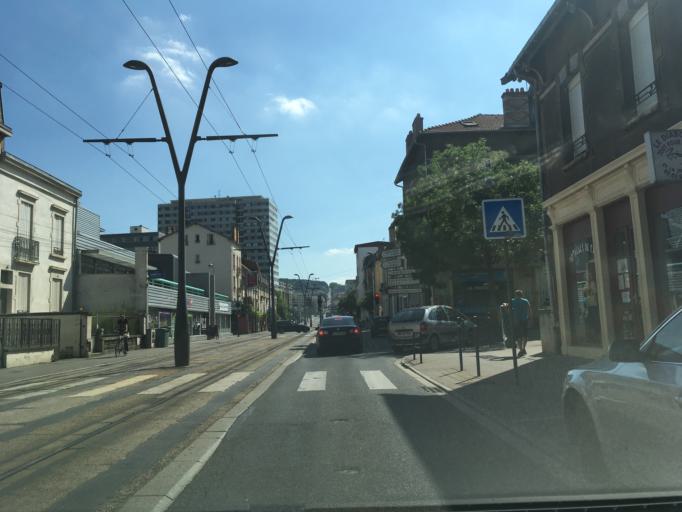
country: FR
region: Lorraine
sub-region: Departement de Meurthe-et-Moselle
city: Villers-les-Nancy
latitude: 48.6701
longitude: 6.1703
